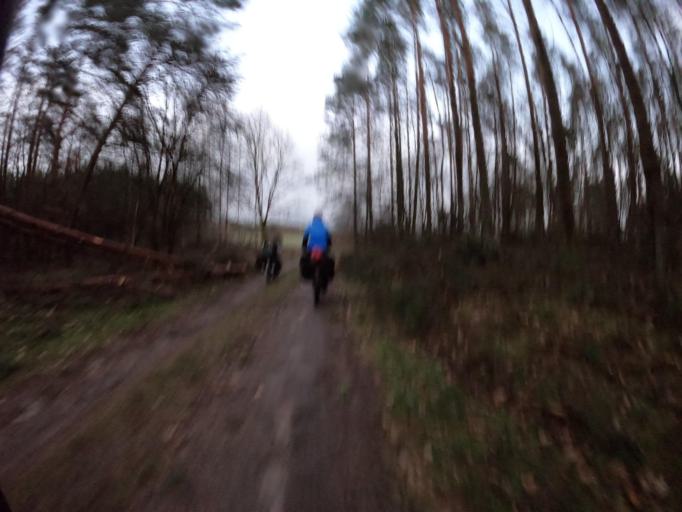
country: PL
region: Greater Poland Voivodeship
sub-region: Powiat zlotowski
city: Sypniewo
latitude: 53.4817
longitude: 16.6371
